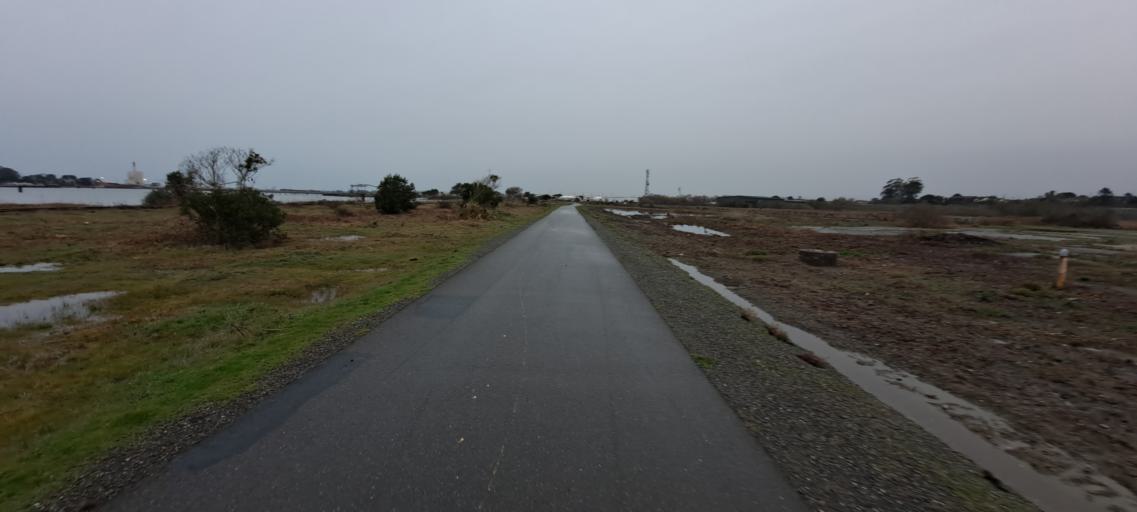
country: US
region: California
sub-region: Humboldt County
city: Bayview
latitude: 40.7854
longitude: -124.1881
